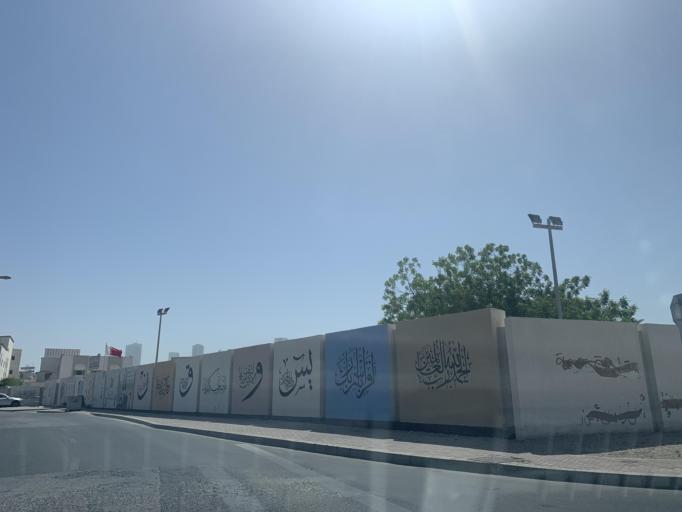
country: BH
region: Manama
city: Jidd Hafs
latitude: 26.2258
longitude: 50.5334
